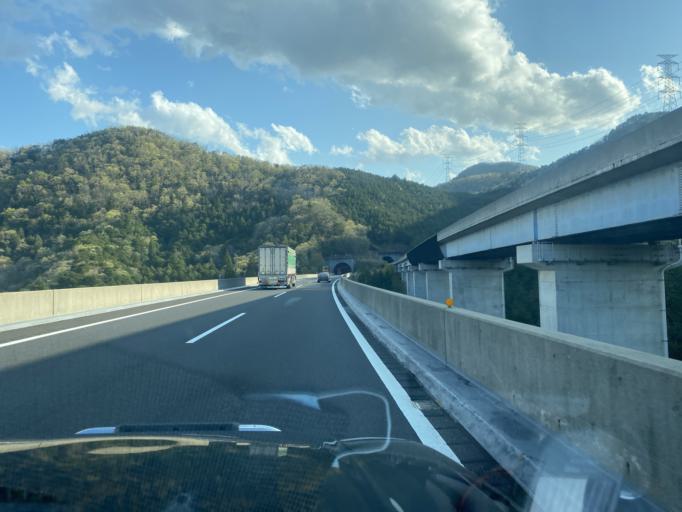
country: JP
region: Hyogo
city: Sasayama
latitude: 34.9832
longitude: 135.1507
